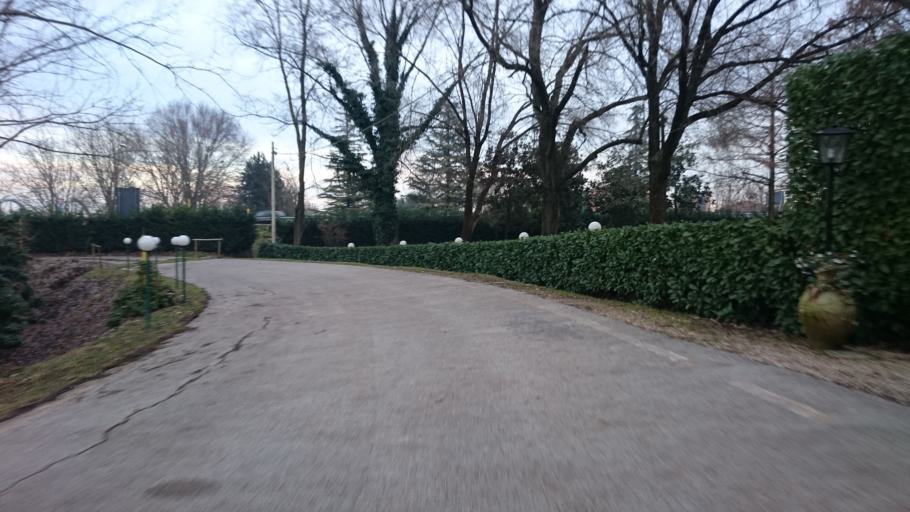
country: IT
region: Veneto
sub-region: Provincia di Padova
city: Saccolongo
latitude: 45.4173
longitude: 11.7235
